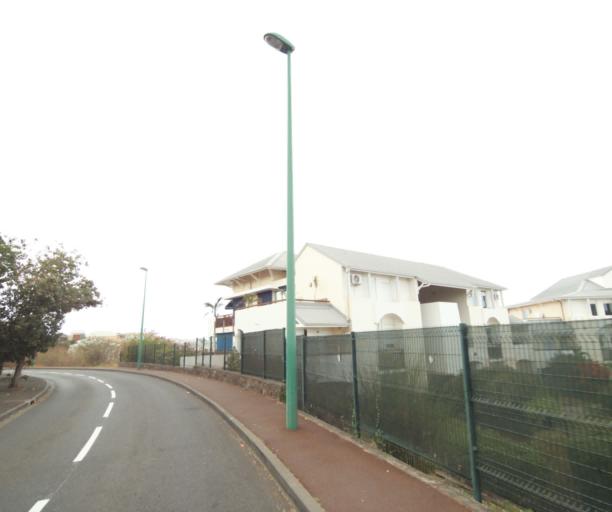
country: RE
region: Reunion
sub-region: Reunion
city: Saint-Paul
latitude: -21.0620
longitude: 55.2293
